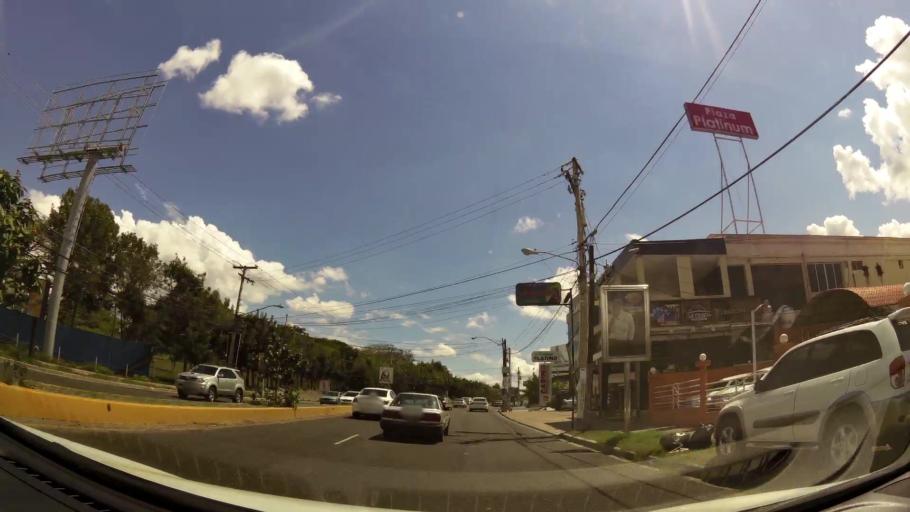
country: DO
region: Santiago
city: Santiago de los Caballeros
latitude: 19.4444
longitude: -70.6875
